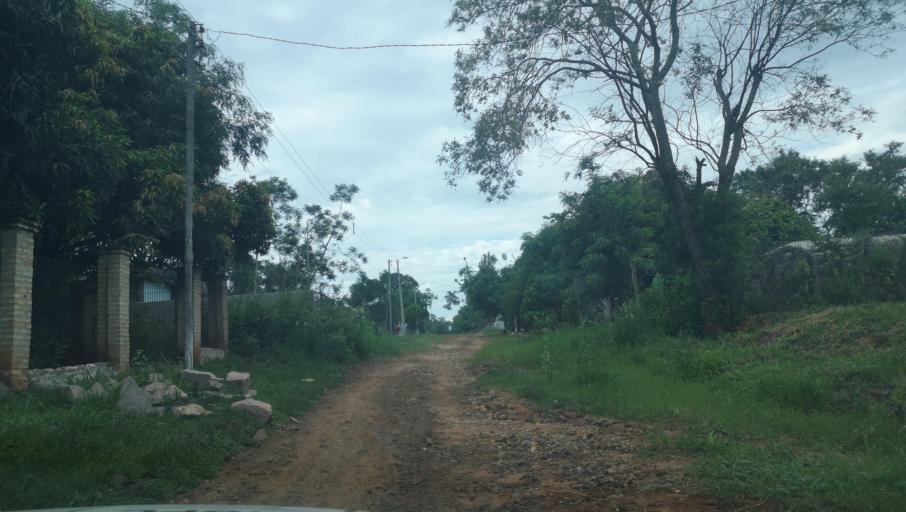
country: PY
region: San Pedro
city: Capiibary
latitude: -24.7417
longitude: -56.0264
